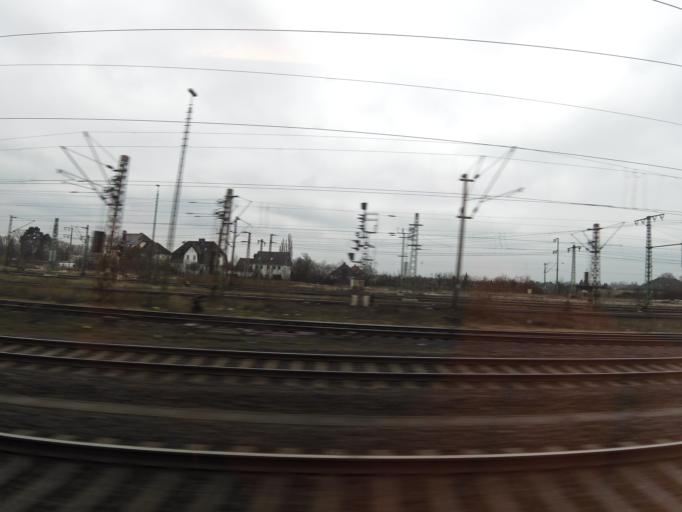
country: DE
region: Lower Saxony
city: Lehrte
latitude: 52.3795
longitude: 9.9614
